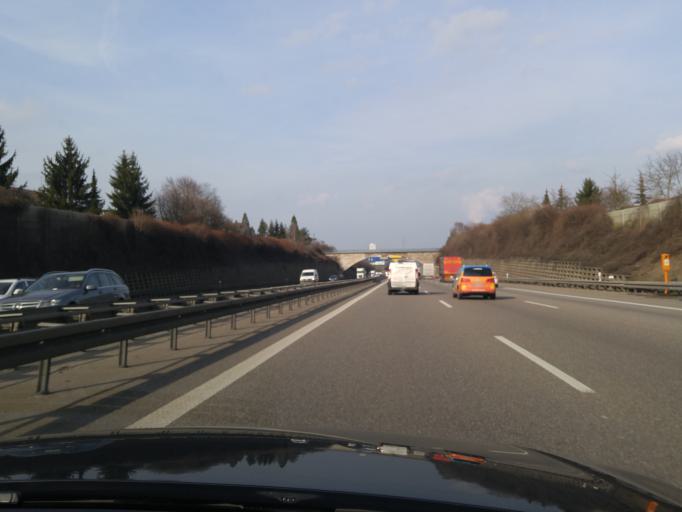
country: DE
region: Baden-Wuerttemberg
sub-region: Regierungsbezirk Stuttgart
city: Asperg
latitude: 48.9060
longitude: 9.1546
